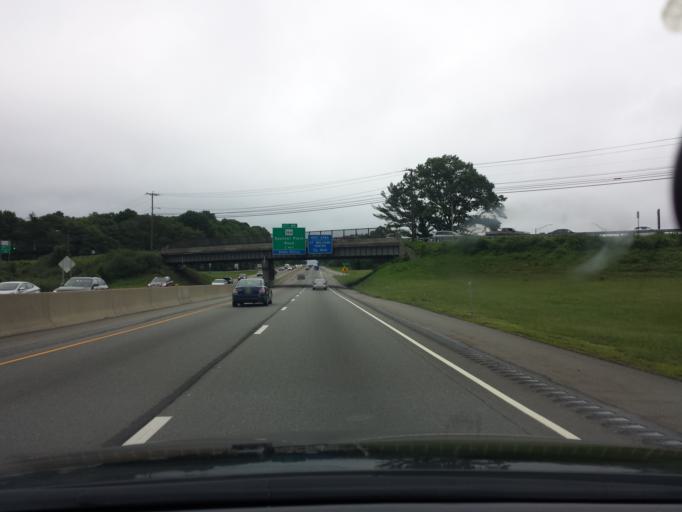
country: US
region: Connecticut
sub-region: Middlesex County
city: Westbrook Center
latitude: 41.2917
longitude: -72.4451
